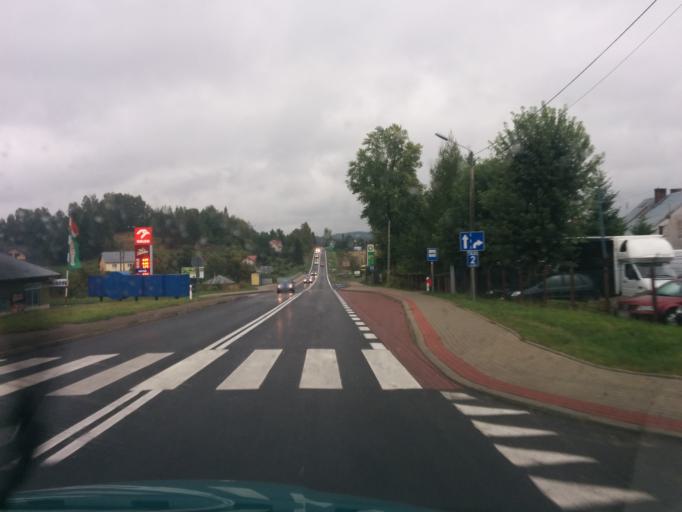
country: PL
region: Subcarpathian Voivodeship
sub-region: Powiat sanocki
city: Sanok
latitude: 49.5370
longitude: 22.2233
